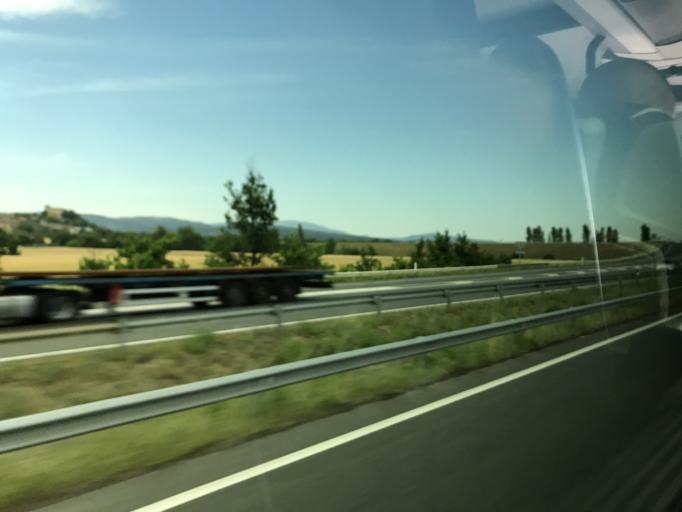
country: ES
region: Basque Country
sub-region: Provincia de Alava
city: Gasteiz / Vitoria
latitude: 42.8589
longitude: -2.7421
